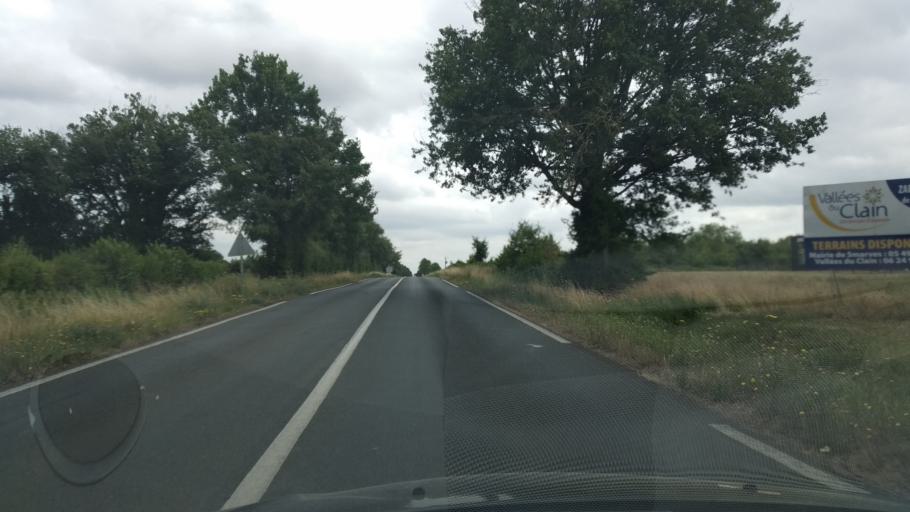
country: FR
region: Poitou-Charentes
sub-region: Departement de la Vienne
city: Smarves
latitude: 46.5041
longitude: 0.3622
